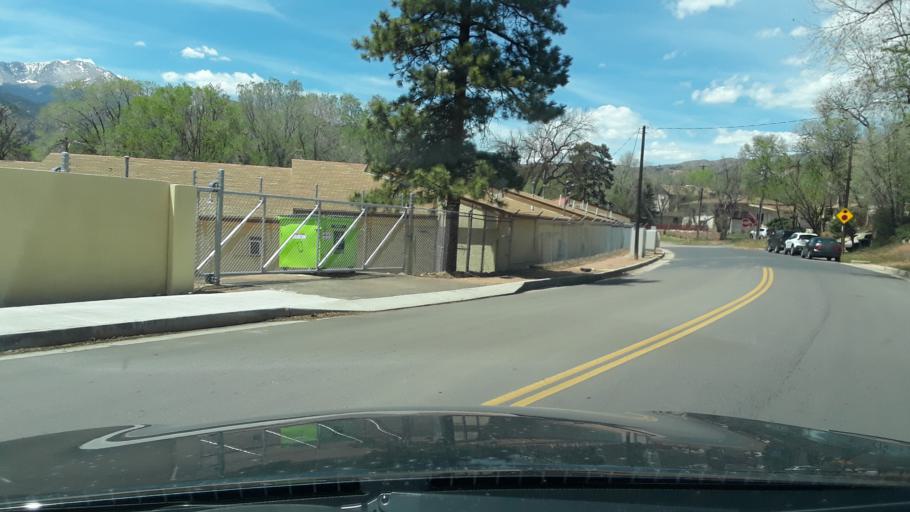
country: US
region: Colorado
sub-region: El Paso County
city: Manitou Springs
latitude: 38.8568
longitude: -104.8818
